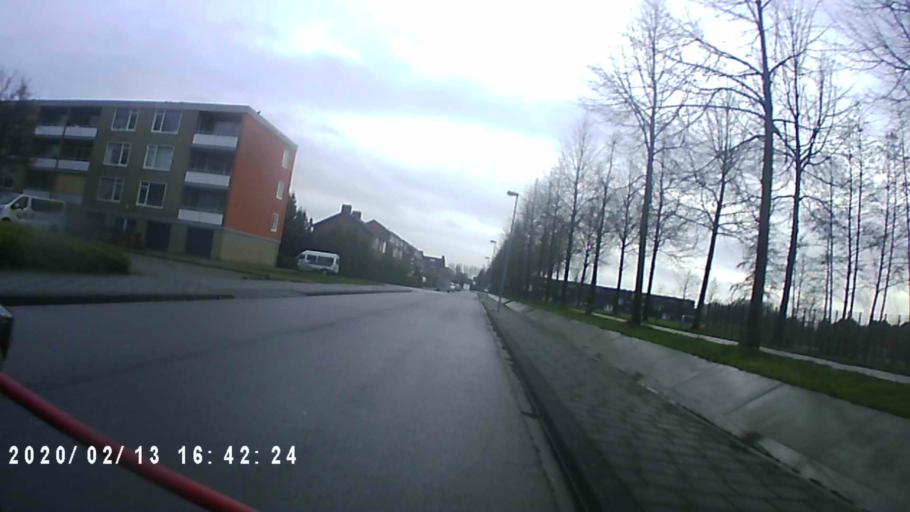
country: NL
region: Groningen
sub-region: Gemeente Groningen
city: Groningen
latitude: 53.2230
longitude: 6.5226
